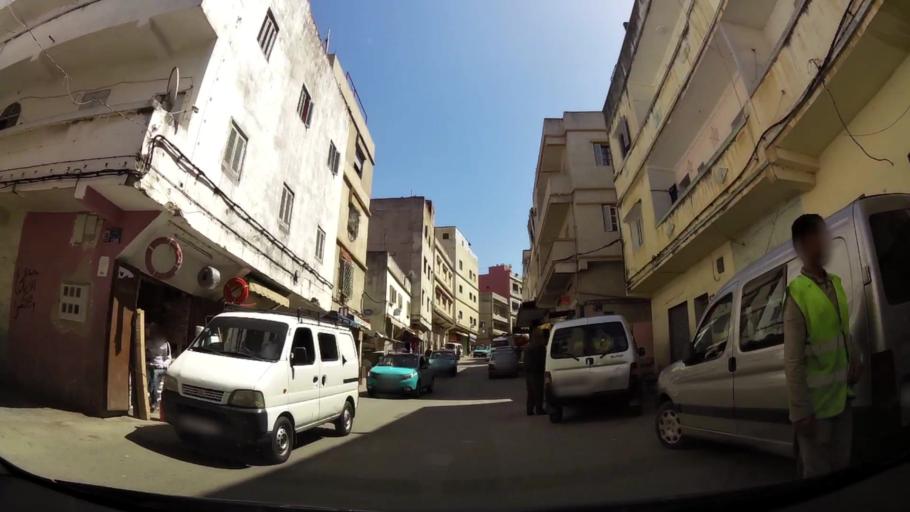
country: MA
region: Tanger-Tetouan
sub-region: Tanger-Assilah
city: Tangier
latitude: 35.7539
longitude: -5.8224
